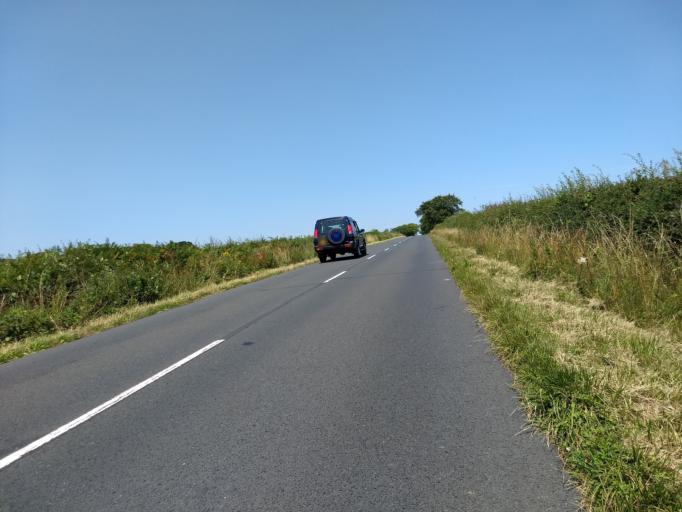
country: GB
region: England
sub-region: Isle of Wight
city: Northwood
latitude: 50.7193
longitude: -1.3527
